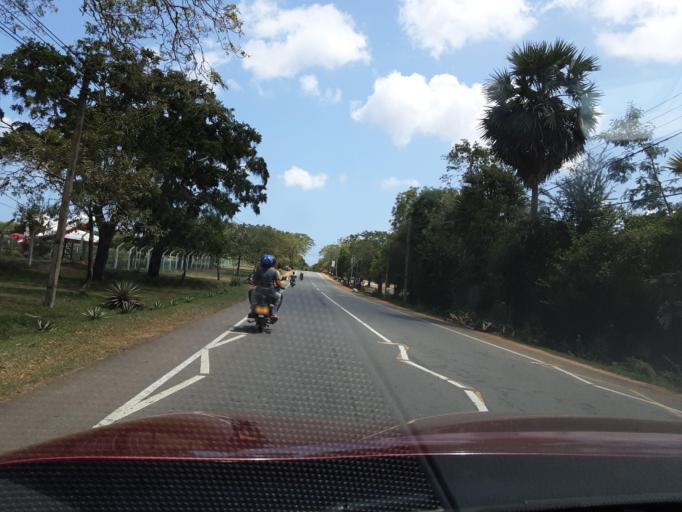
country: LK
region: Southern
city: Tangalla
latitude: 6.2532
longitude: 81.2274
